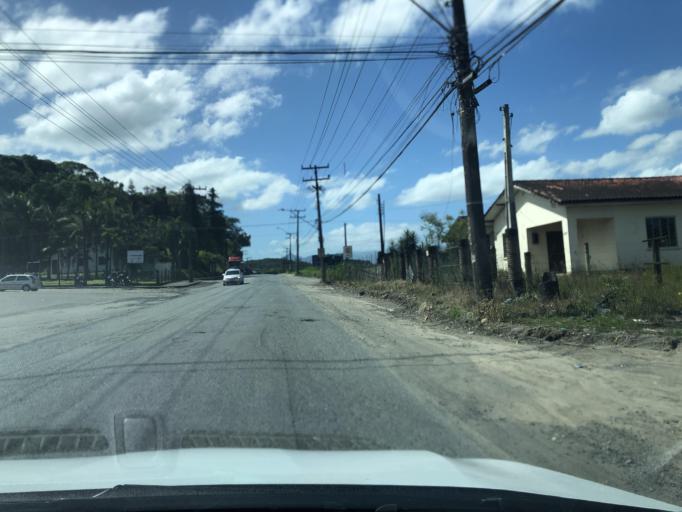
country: BR
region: Santa Catarina
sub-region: Joinville
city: Joinville
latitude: -26.2590
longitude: -48.8670
